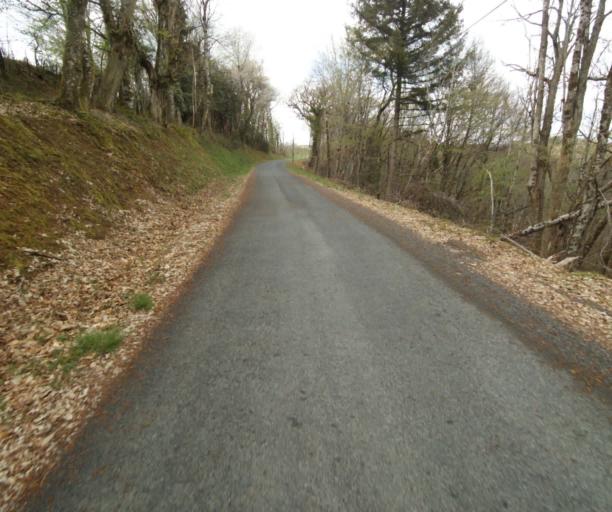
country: FR
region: Limousin
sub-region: Departement de la Correze
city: Sainte-Fortunade
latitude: 45.1923
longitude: 1.8630
